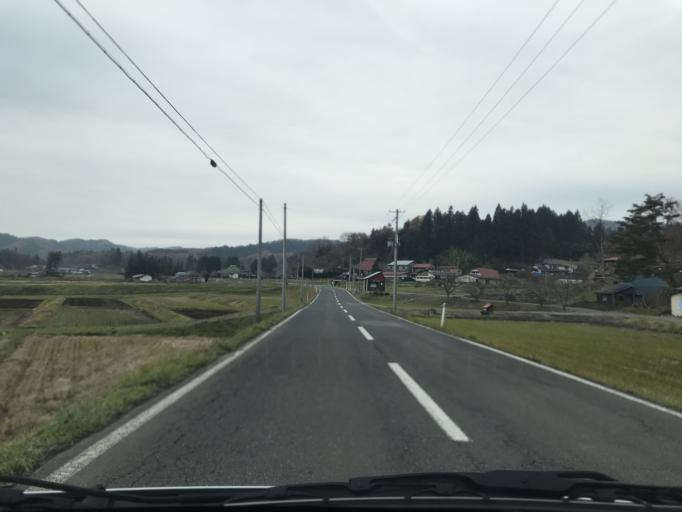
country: JP
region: Iwate
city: Kitakami
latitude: 39.2591
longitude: 141.2010
